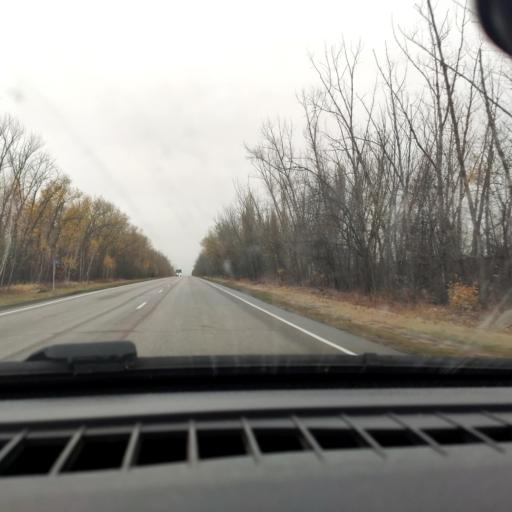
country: RU
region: Voronezj
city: Ostrogozhsk
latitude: 51.0106
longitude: 38.9940
